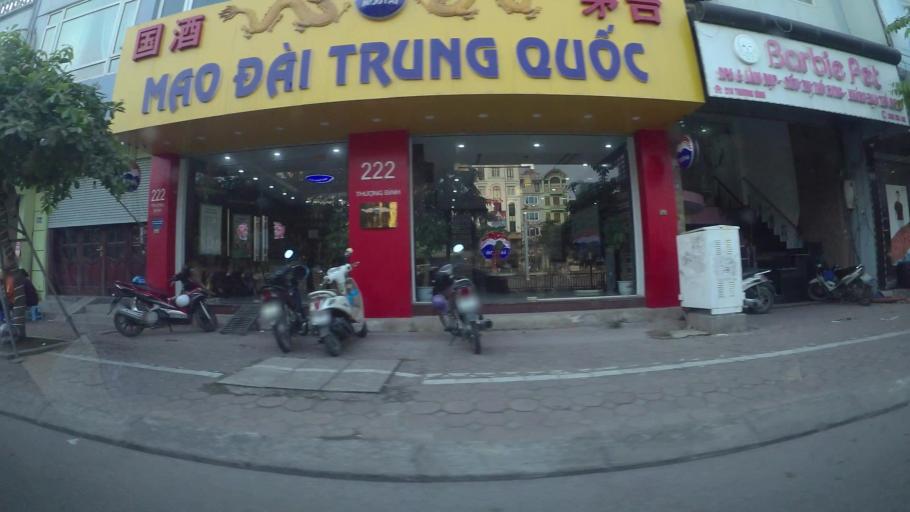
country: VN
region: Ha Noi
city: Thanh Xuan
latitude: 20.9970
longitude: 105.8156
